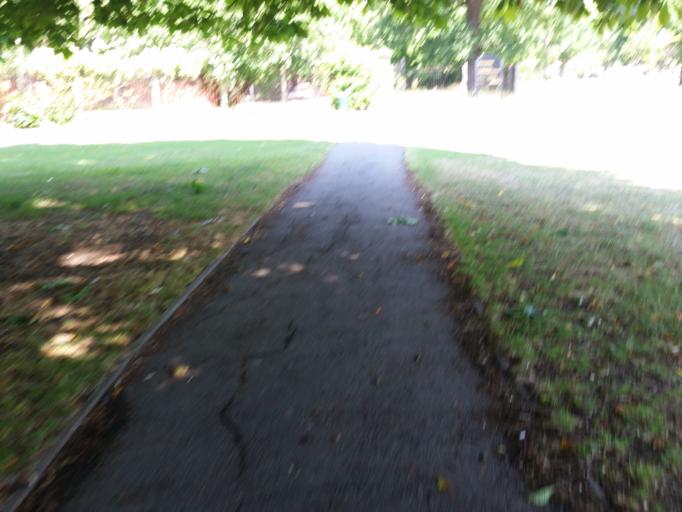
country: GB
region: England
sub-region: Greater London
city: Harringay
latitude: 51.6006
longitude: -0.0751
